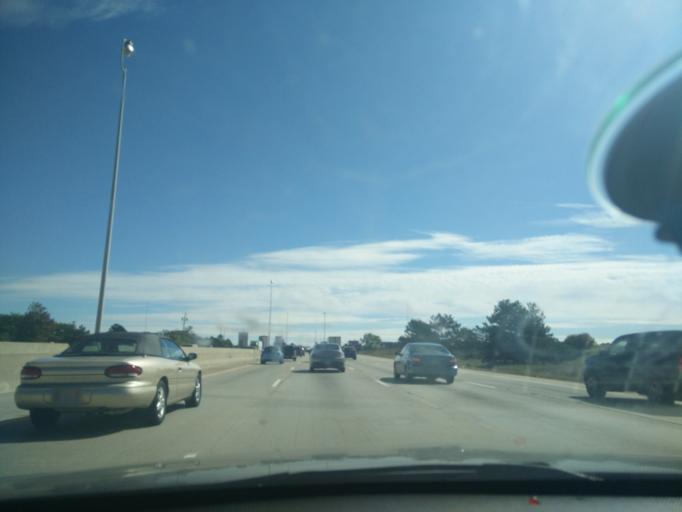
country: US
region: Michigan
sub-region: Oakland County
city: Bingham Farms
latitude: 42.4873
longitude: -83.2785
